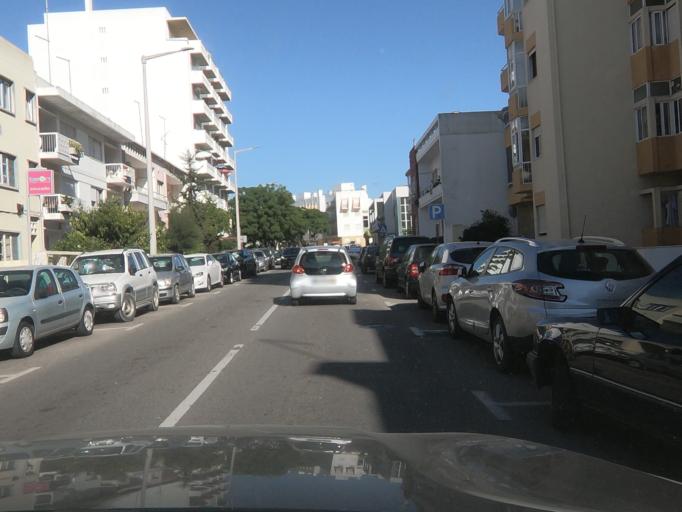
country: PT
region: Faro
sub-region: Loule
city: Loule
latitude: 37.1404
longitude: -8.0201
